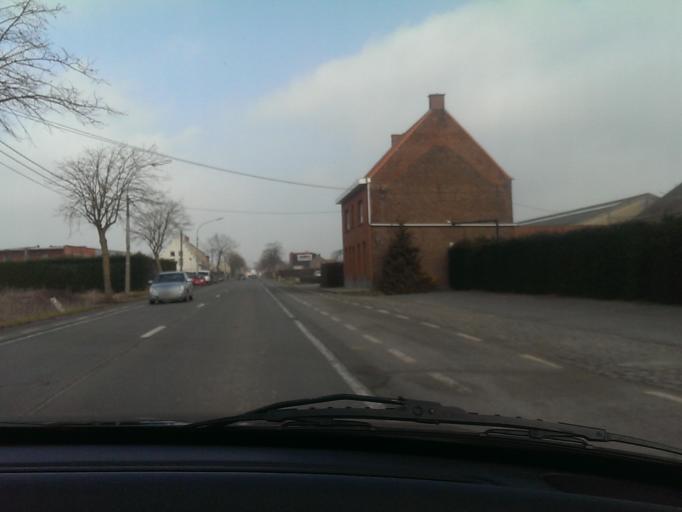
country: BE
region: Flanders
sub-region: Provincie West-Vlaanderen
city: Roeselare
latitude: 50.9100
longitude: 3.1157
